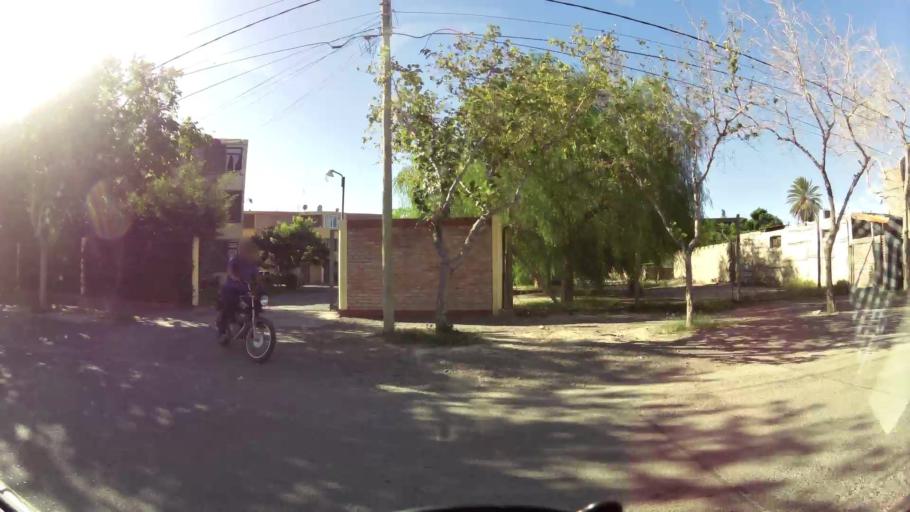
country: AR
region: San Juan
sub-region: Departamento de Santa Lucia
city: Santa Lucia
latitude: -31.5343
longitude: -68.5092
